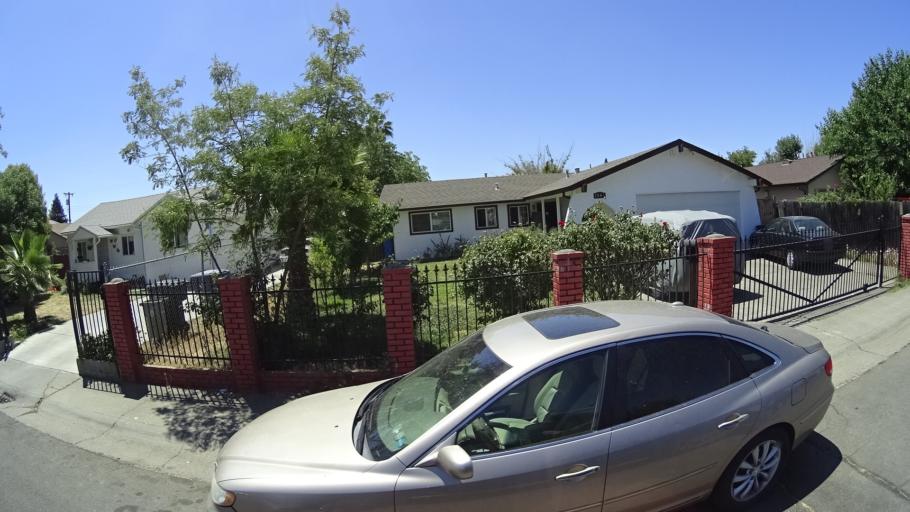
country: US
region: California
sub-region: Sacramento County
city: Florin
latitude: 38.5179
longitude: -121.4111
